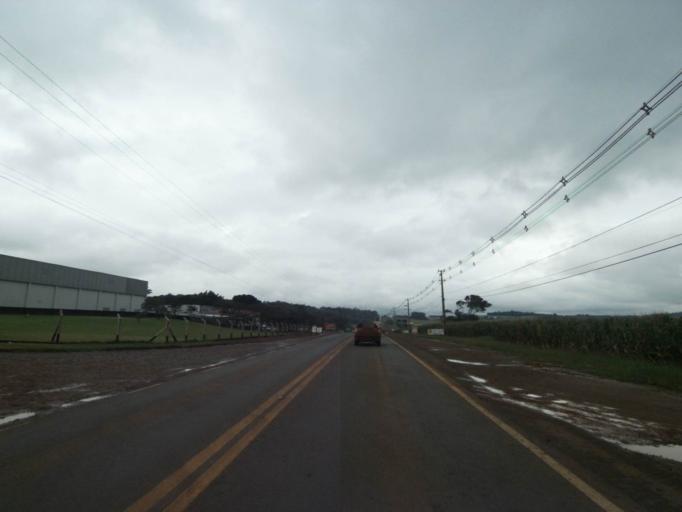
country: BR
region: Parana
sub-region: Marechal Candido Rondon
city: Marechal Candido Rondon
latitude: -24.5684
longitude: -54.0267
